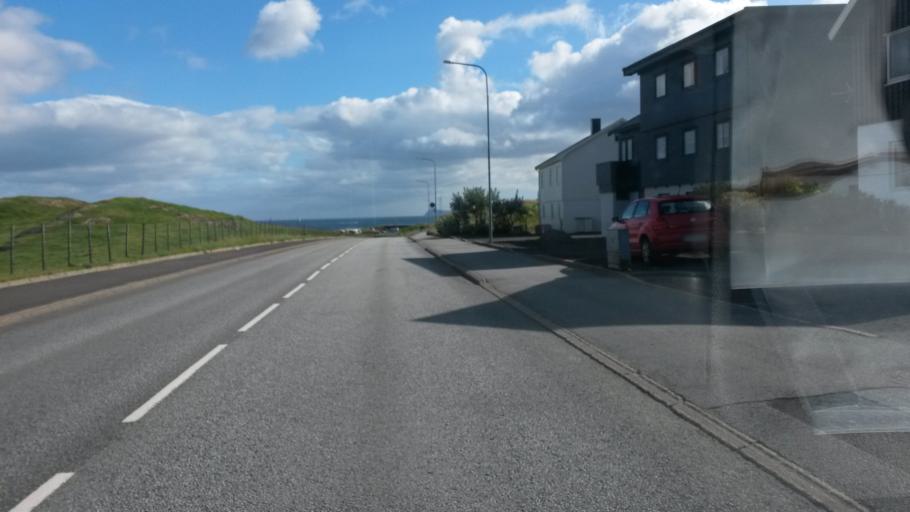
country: FO
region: Streymoy
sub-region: Torshavn
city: Torshavn
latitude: 62.0198
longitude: -6.7573
